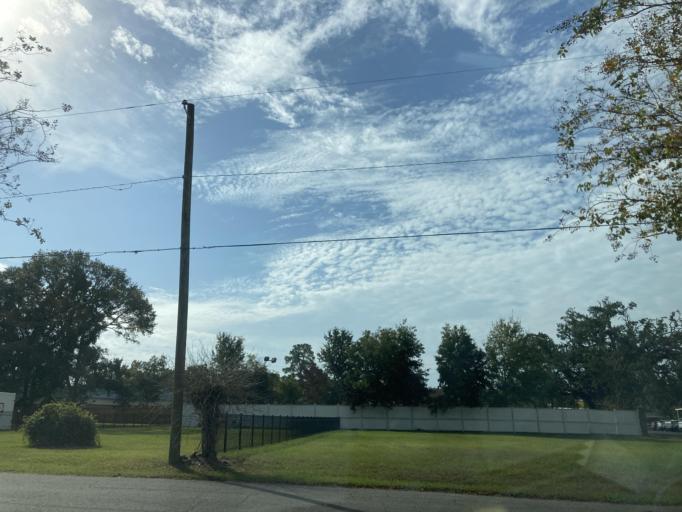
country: US
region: Mississippi
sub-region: Jackson County
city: Ocean Springs
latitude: 30.4173
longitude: -88.8296
